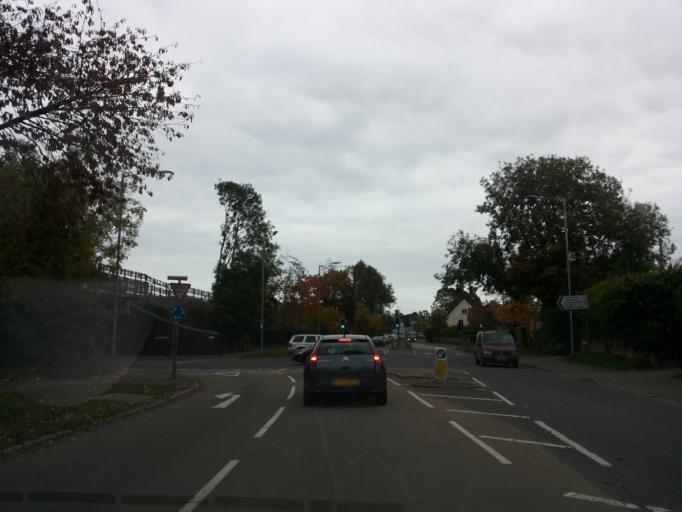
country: GB
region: England
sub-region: Buckinghamshire
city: Amersham on the Hill
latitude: 51.6728
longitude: -0.5924
